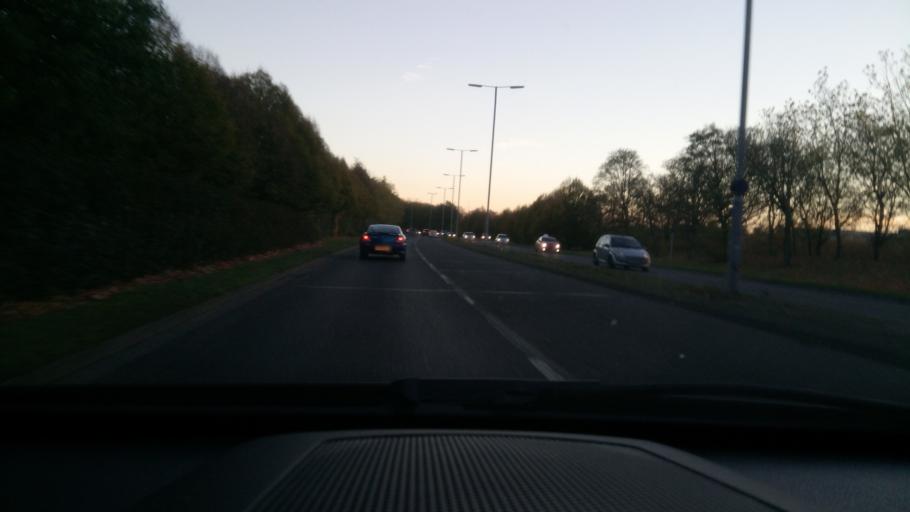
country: GB
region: England
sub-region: Peterborough
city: Peterborough
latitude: 52.5892
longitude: -0.2559
